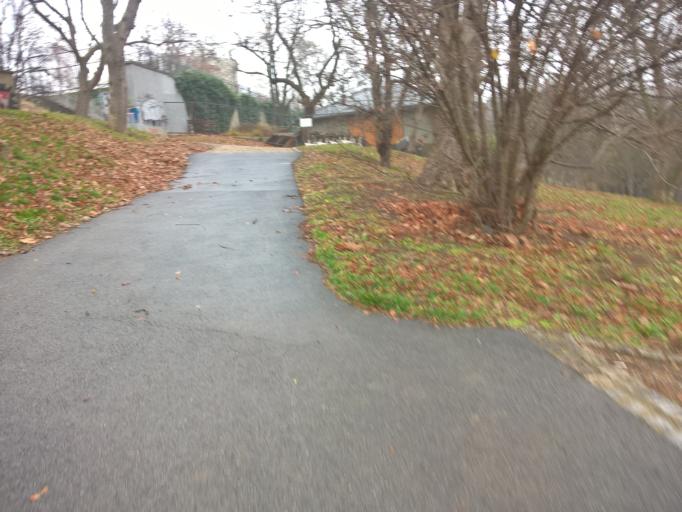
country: CZ
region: Praha
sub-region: Praha 1
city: Mala Strana
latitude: 50.0786
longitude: 14.3946
